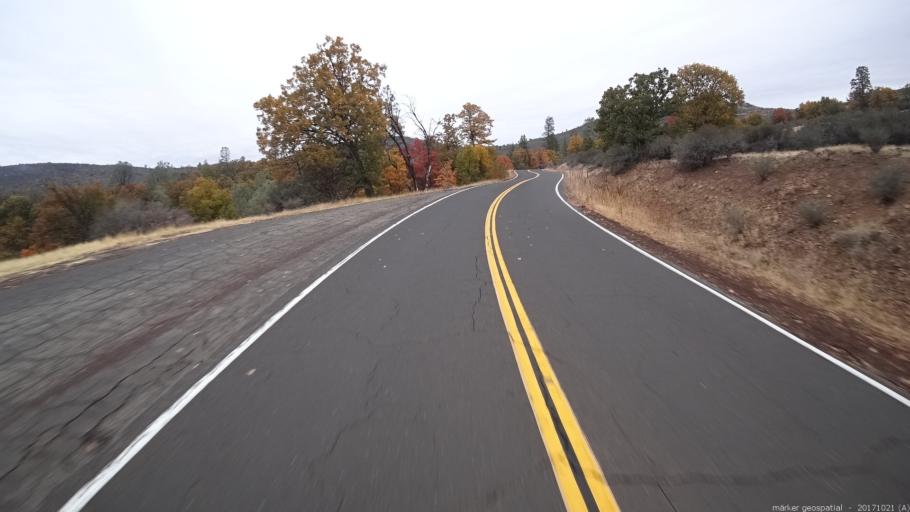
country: US
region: California
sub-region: Shasta County
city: Burney
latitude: 40.9947
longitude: -121.5042
